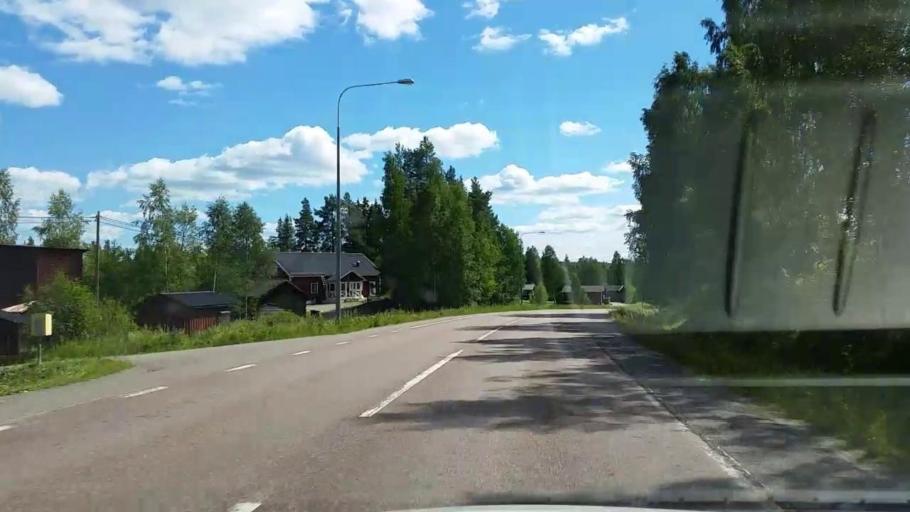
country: SE
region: Dalarna
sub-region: Faluns Kommun
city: Svardsjo
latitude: 60.8267
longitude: 15.7611
